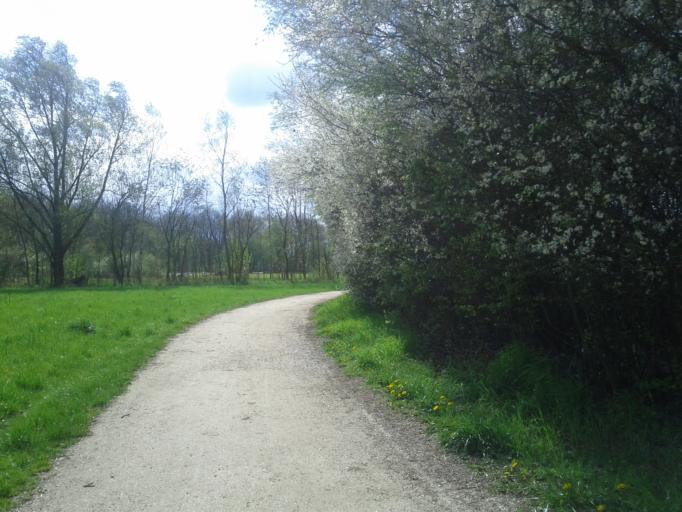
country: DE
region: North Rhine-Westphalia
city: Lanstrop
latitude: 51.5528
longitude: 7.5626
